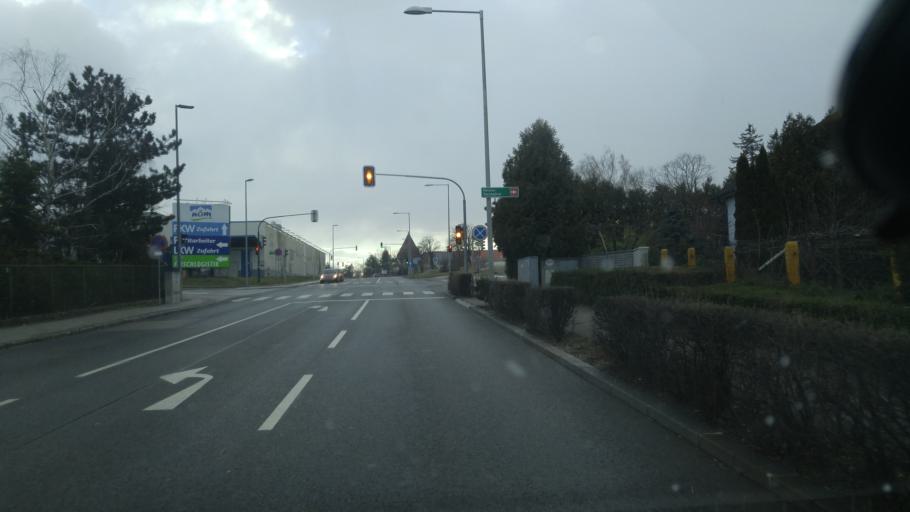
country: AT
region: Lower Austria
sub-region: Politischer Bezirk Baden
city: Baden
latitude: 47.9946
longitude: 16.2265
